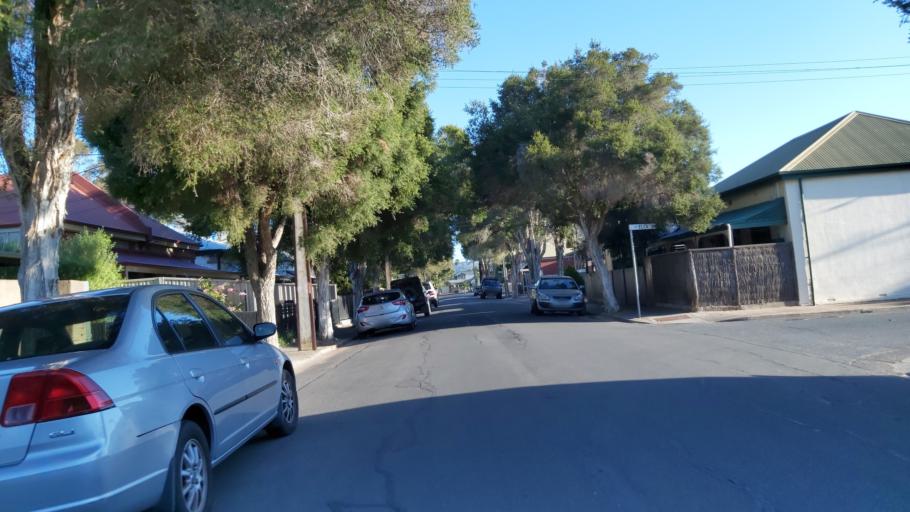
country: AU
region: South Australia
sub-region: Unley
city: Unley
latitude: -34.9459
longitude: 138.6101
